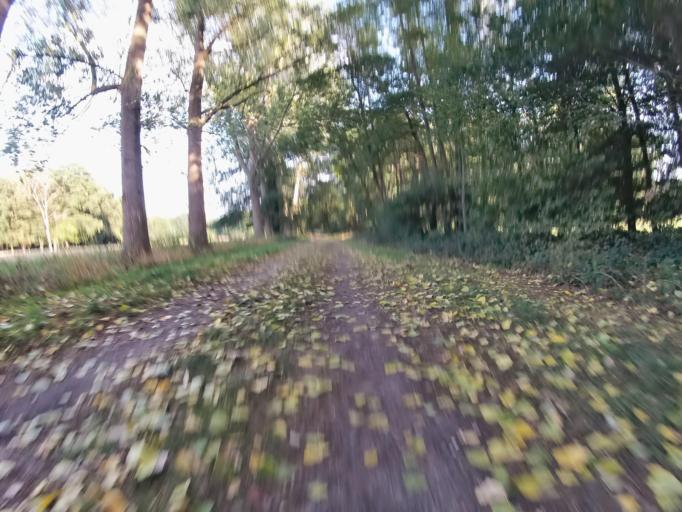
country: DE
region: North Rhine-Westphalia
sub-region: Regierungsbezirk Munster
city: Westerkappeln
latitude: 52.3189
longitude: 7.8384
